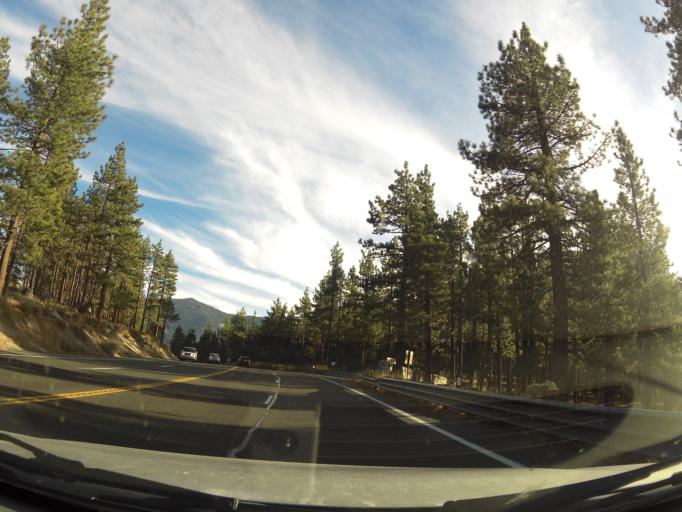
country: US
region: Nevada
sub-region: Douglas County
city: Kingsbury
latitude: 38.9890
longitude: -119.9492
